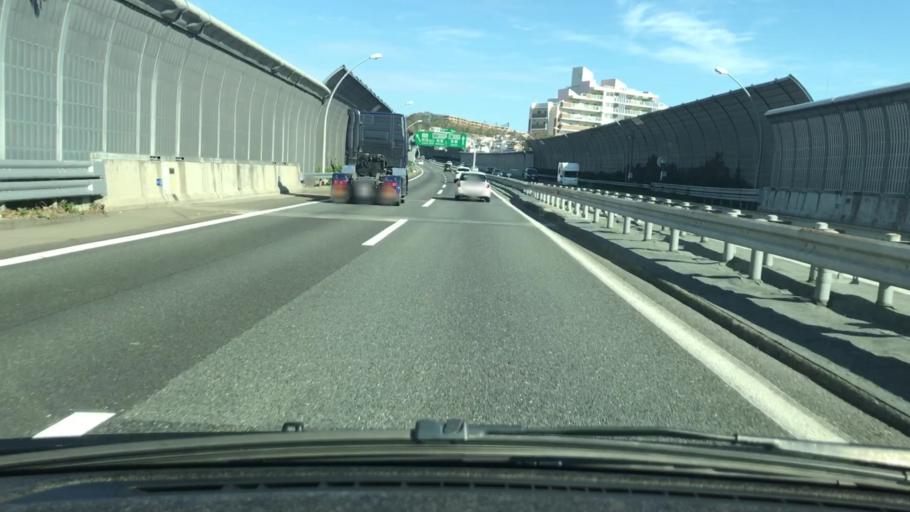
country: JP
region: Osaka
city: Suita
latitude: 34.7913
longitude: 135.5350
